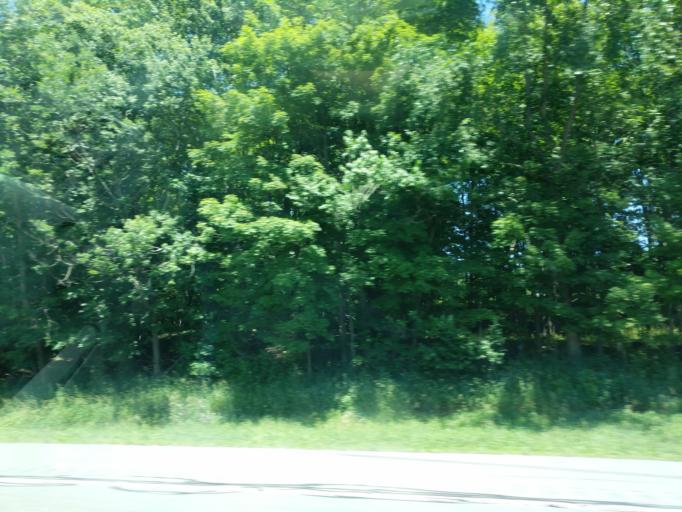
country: US
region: New York
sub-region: Sullivan County
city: Rock Hill
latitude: 41.6285
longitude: -74.6066
